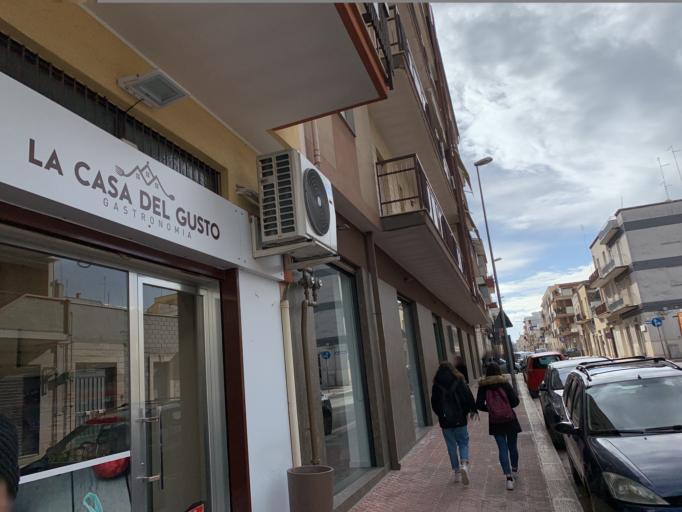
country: IT
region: Apulia
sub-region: Provincia di Barletta - Andria - Trani
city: Andria
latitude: 41.2345
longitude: 16.2947
